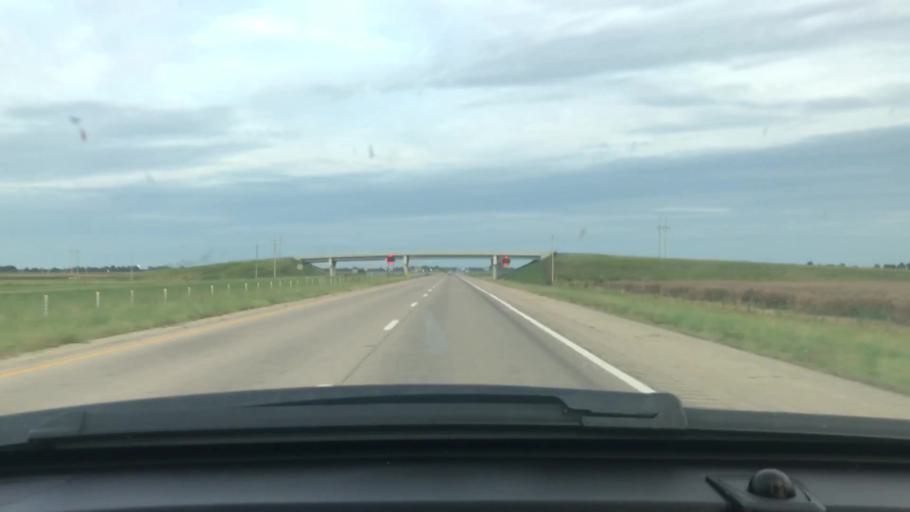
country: US
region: Arkansas
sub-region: Craighead County
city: Bay
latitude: 35.7071
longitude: -90.5688
